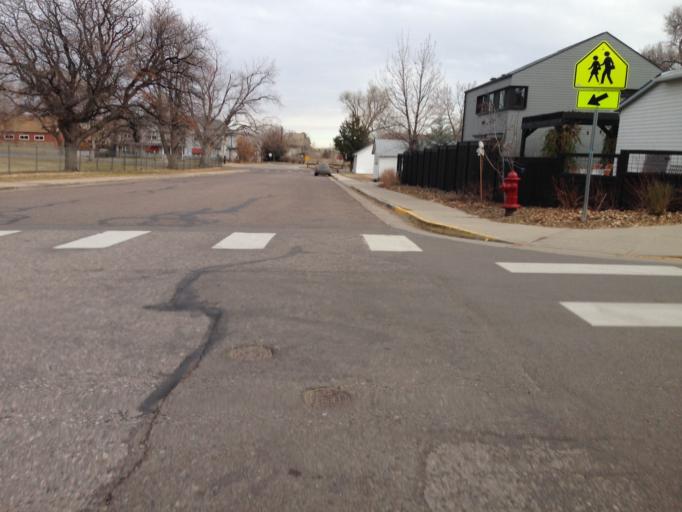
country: US
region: Colorado
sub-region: Boulder County
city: Louisville
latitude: 39.9826
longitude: -105.1335
